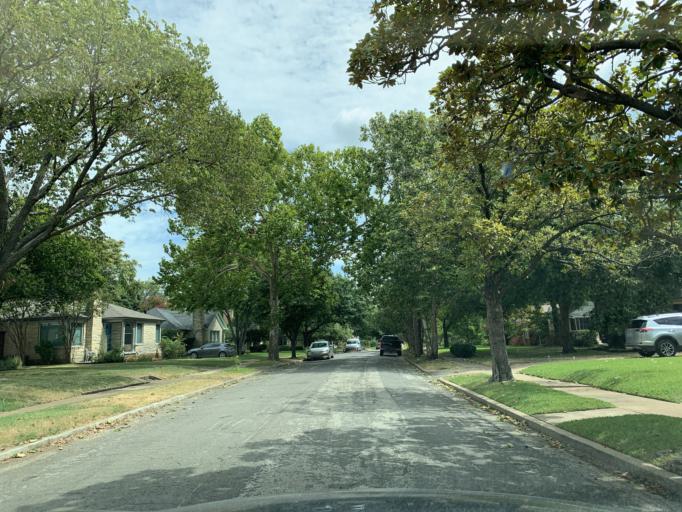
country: US
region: Texas
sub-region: Dallas County
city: Cockrell Hill
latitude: 32.7620
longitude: -96.8618
